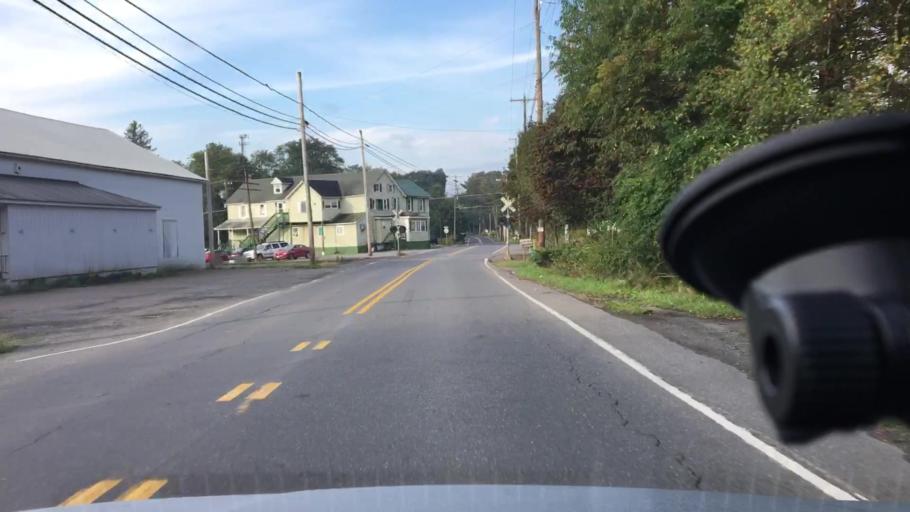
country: US
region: Pennsylvania
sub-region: Monroe County
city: Mount Pocono
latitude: 41.1152
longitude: -75.3863
